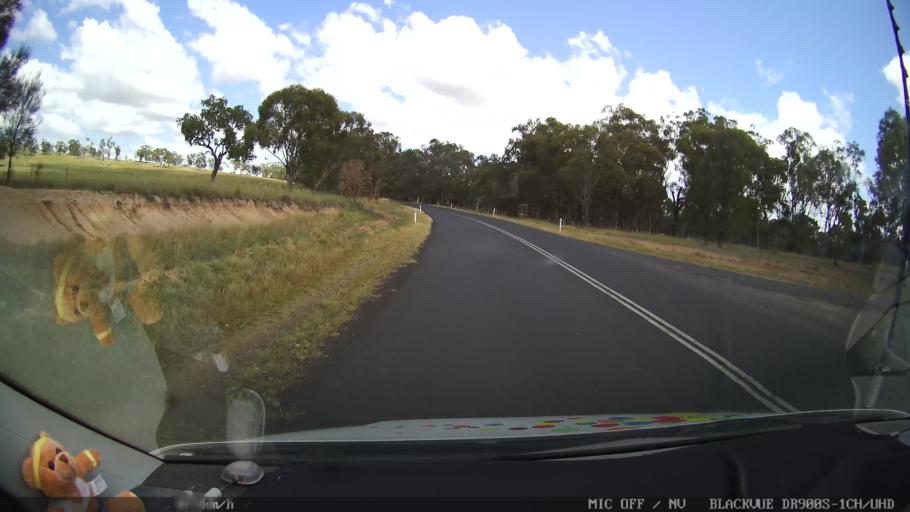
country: AU
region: New South Wales
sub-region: Glen Innes Severn
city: Glen Innes
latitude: -29.4747
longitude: 151.6806
